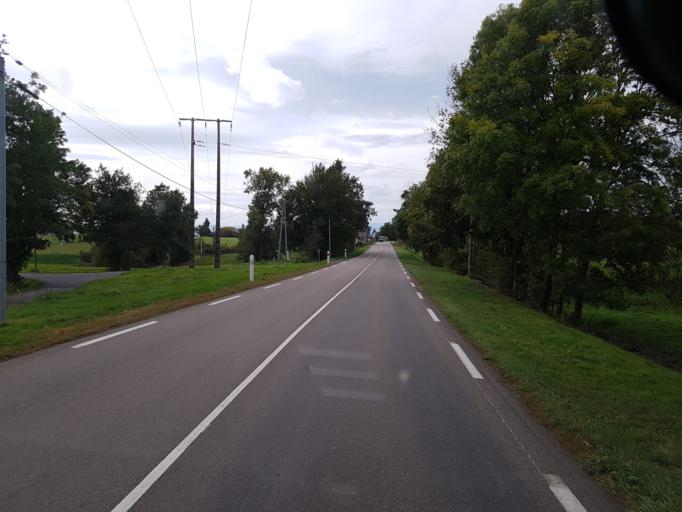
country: FR
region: Rhone-Alpes
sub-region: Departement de la Loire
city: Saint-Galmier
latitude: 45.6237
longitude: 4.3482
